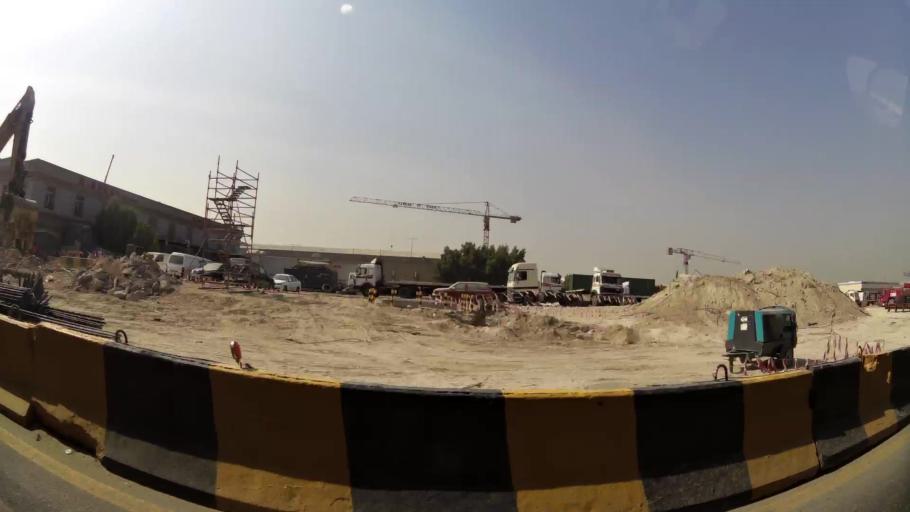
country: KW
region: Al Asimah
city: Ar Rabiyah
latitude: 29.3287
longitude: 47.9326
